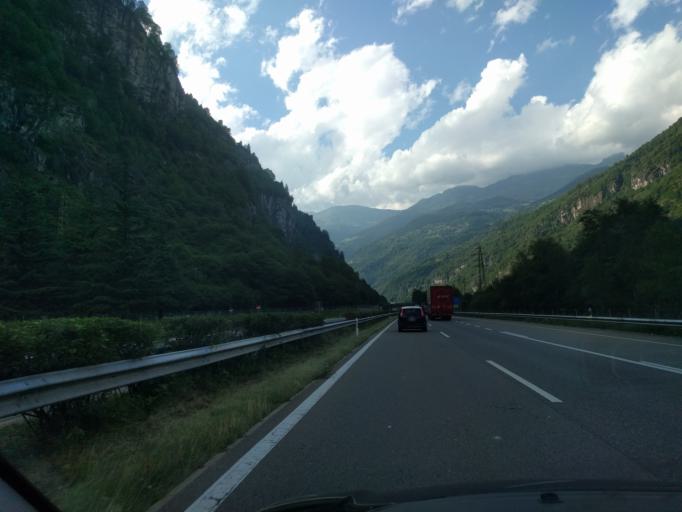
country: CH
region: Ticino
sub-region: Leventina District
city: Faido
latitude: 46.4480
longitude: 8.8302
